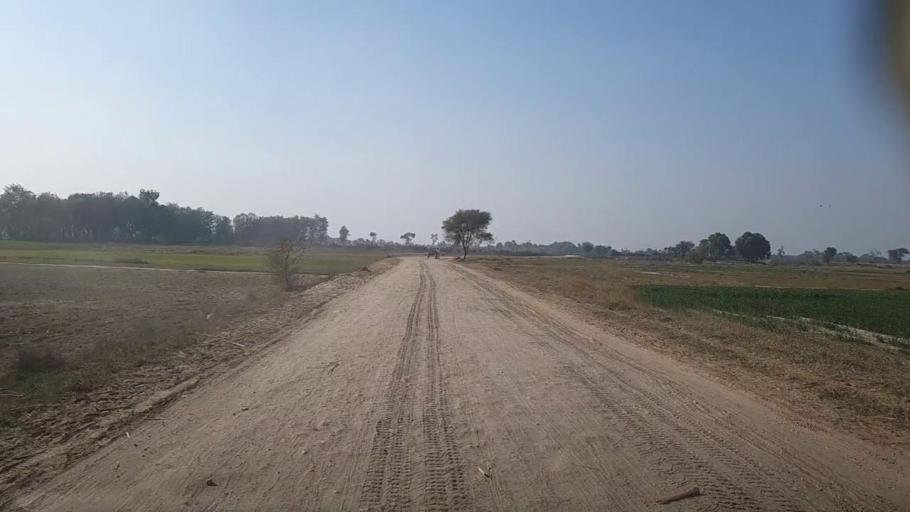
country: PK
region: Sindh
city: Mirpur Mathelo
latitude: 27.8988
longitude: 69.6473
